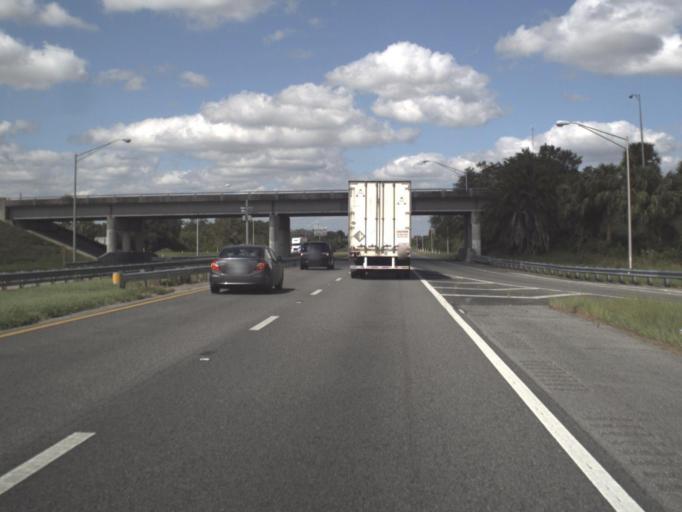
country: US
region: Florida
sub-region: Osceola County
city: Buenaventura Lakes
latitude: 28.2888
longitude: -81.3460
